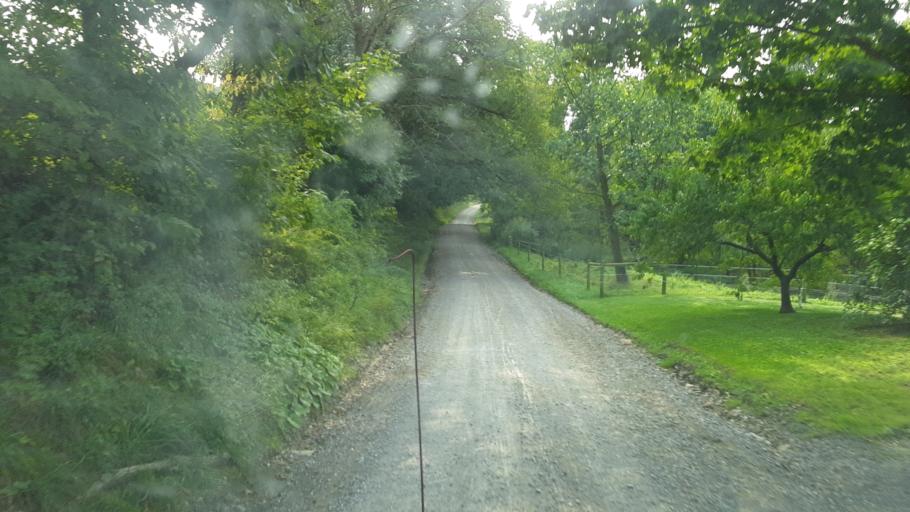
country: US
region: Ohio
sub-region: Holmes County
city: Millersburg
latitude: 40.4397
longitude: -81.8351
